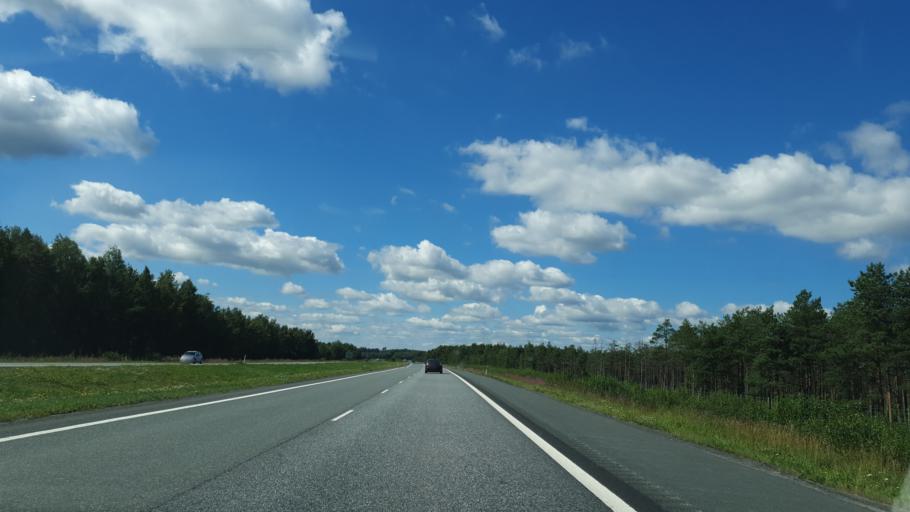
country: FI
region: Haeme
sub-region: Haemeenlinna
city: Kalvola
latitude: 61.1414
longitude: 24.0482
